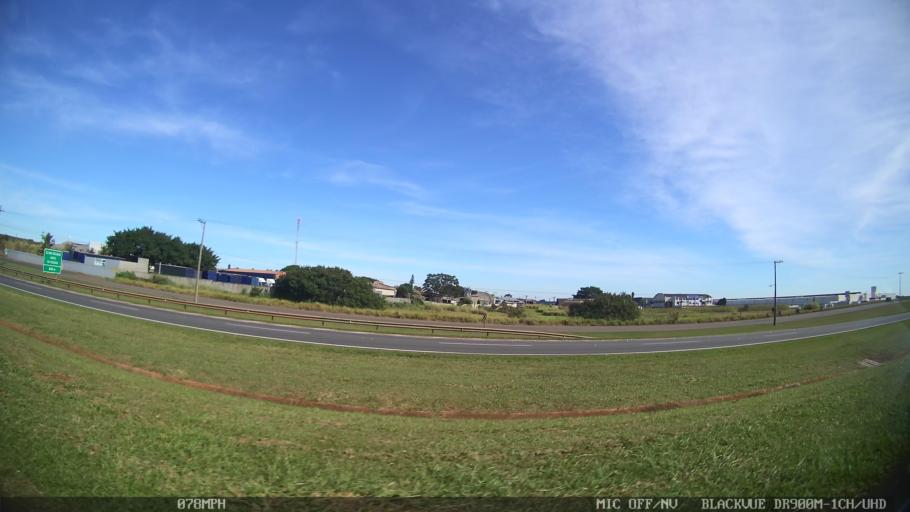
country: BR
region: Sao Paulo
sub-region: Cordeiropolis
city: Cordeiropolis
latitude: -22.4959
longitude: -47.3993
